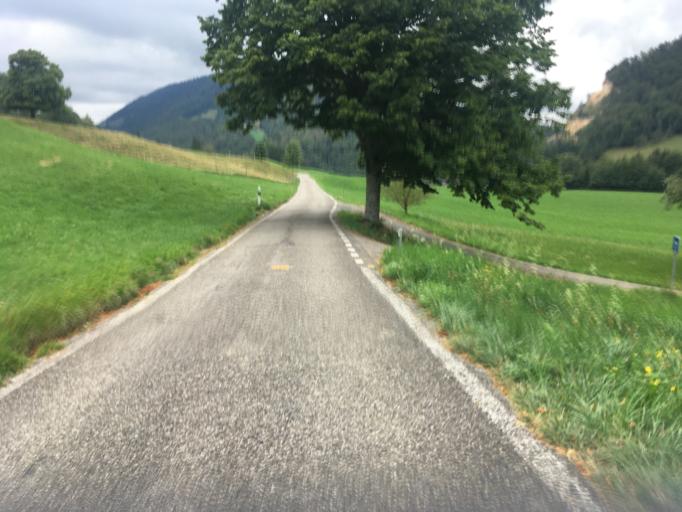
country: CH
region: Solothurn
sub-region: Bezirk Thal
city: Welschenrohr
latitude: 47.2623
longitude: 7.4782
